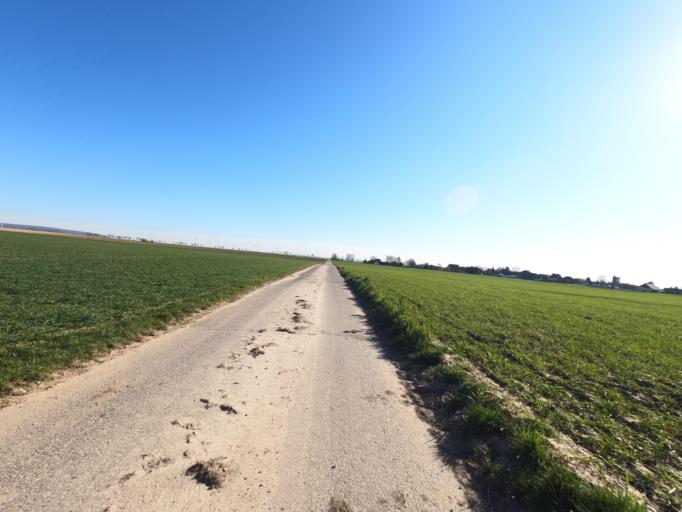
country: DE
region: North Rhine-Westphalia
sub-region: Regierungsbezirk Koln
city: Linnich
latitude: 51.0052
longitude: 6.3239
